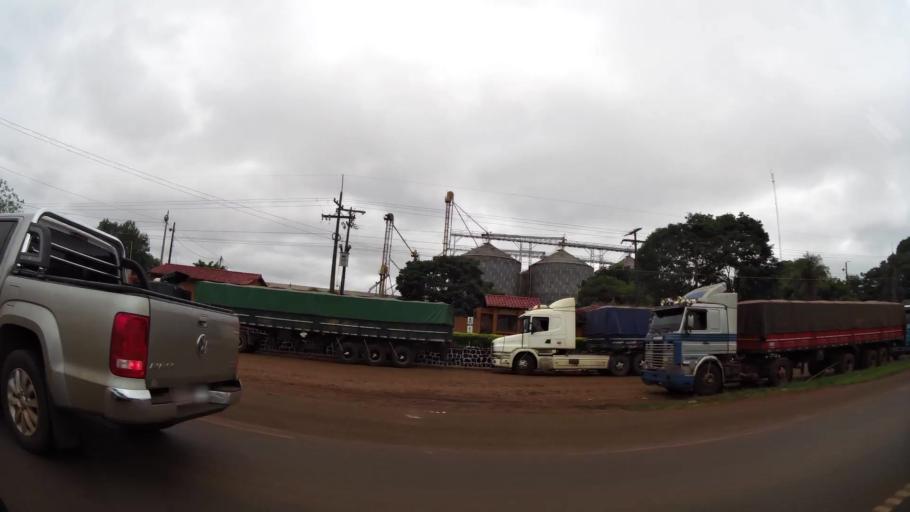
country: PY
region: Alto Parana
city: Colonia Yguazu
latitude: -25.4889
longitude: -54.8114
